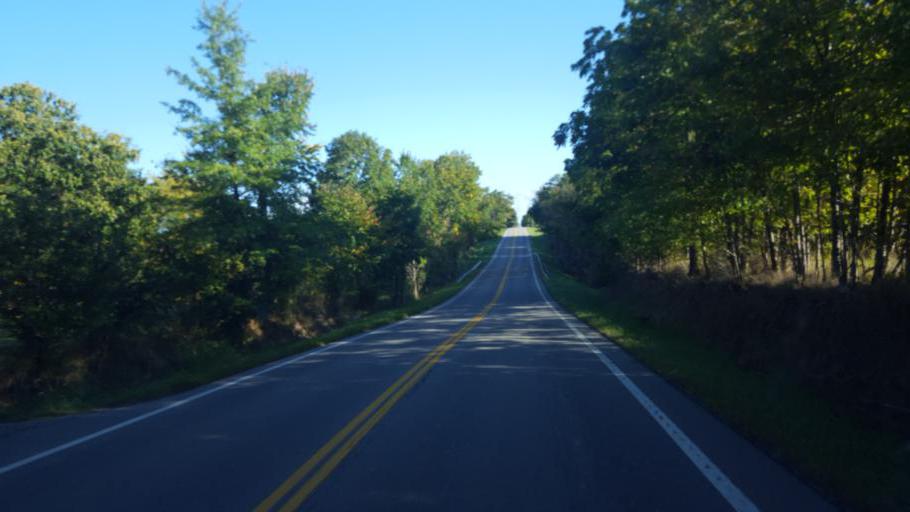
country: US
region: Ohio
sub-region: Lorain County
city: Camden
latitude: 41.1629
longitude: -82.3097
